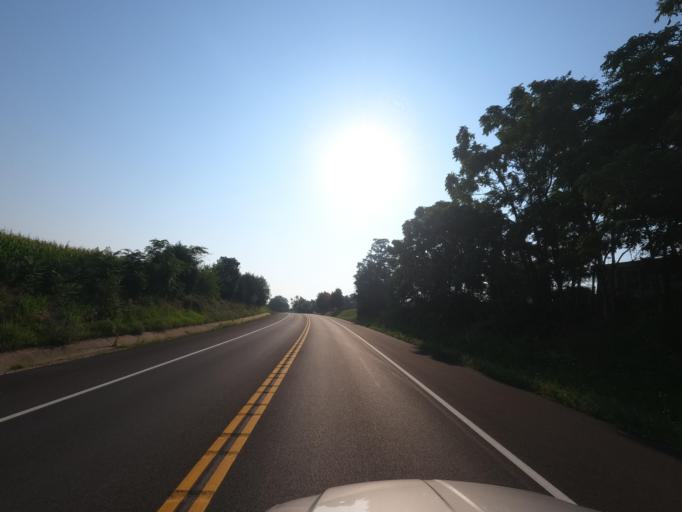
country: US
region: Maryland
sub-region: Washington County
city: Smithsburg
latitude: 39.6963
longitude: -77.6162
